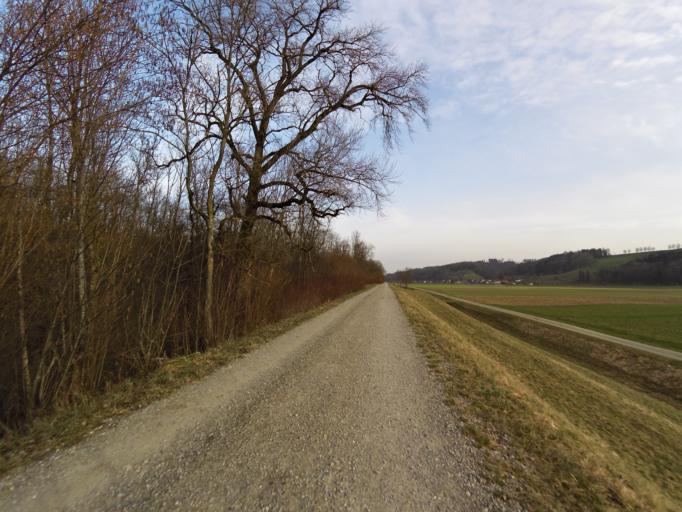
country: CH
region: Thurgau
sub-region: Frauenfeld District
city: Mullheim
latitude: 47.5863
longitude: 8.9918
